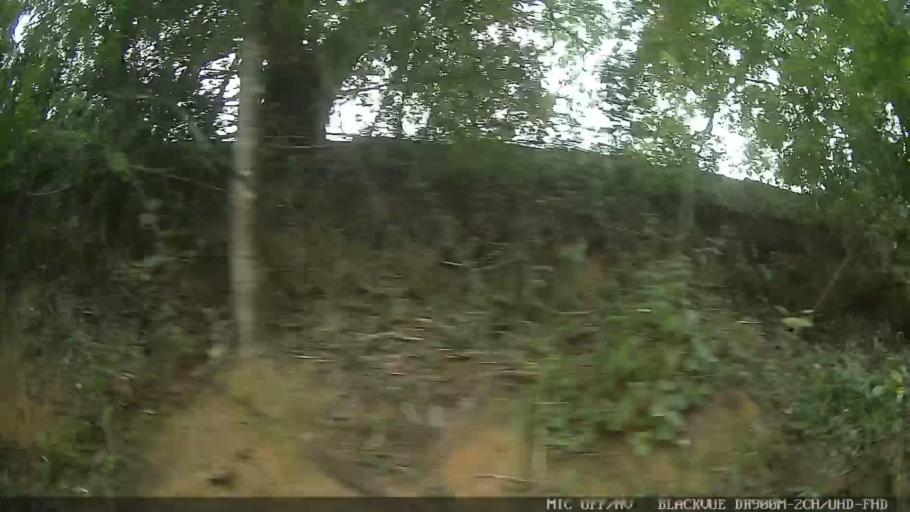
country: BR
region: Sao Paulo
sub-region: Atibaia
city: Atibaia
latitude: -23.1571
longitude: -46.5670
